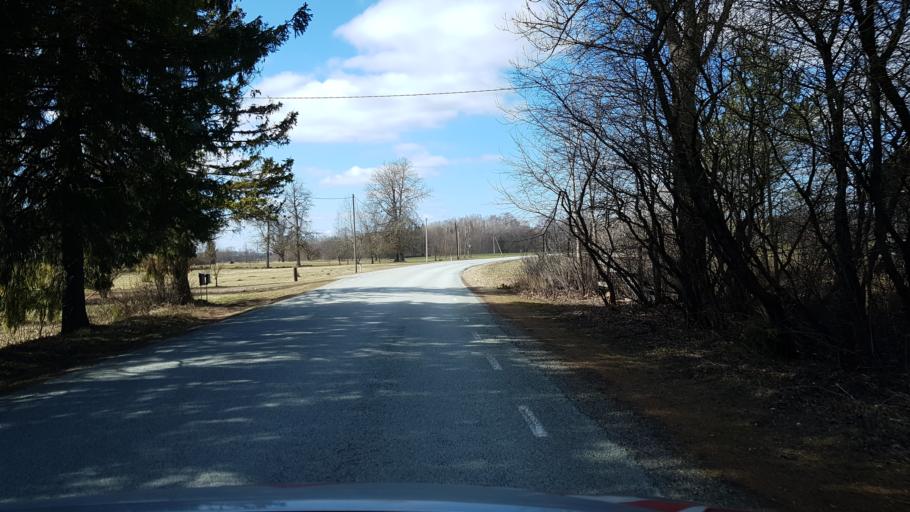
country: EE
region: Laeaene-Virumaa
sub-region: Tapa vald
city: Tapa
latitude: 59.2516
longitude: 25.7421
